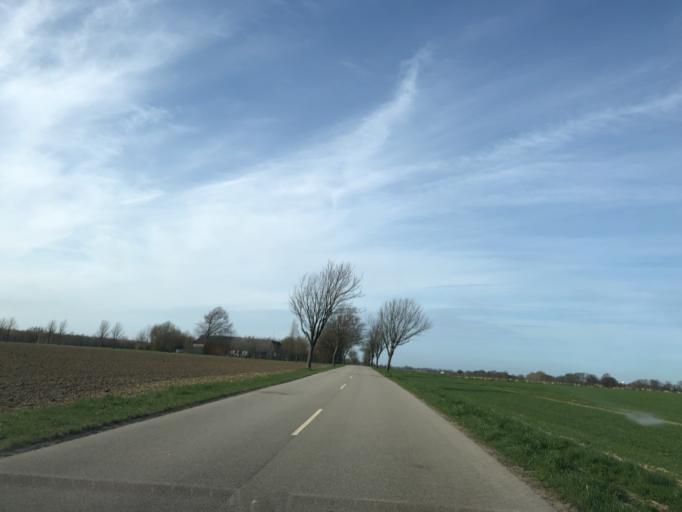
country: DK
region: Zealand
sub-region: Stevns Kommune
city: Store Heddinge
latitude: 55.3046
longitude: 12.4383
